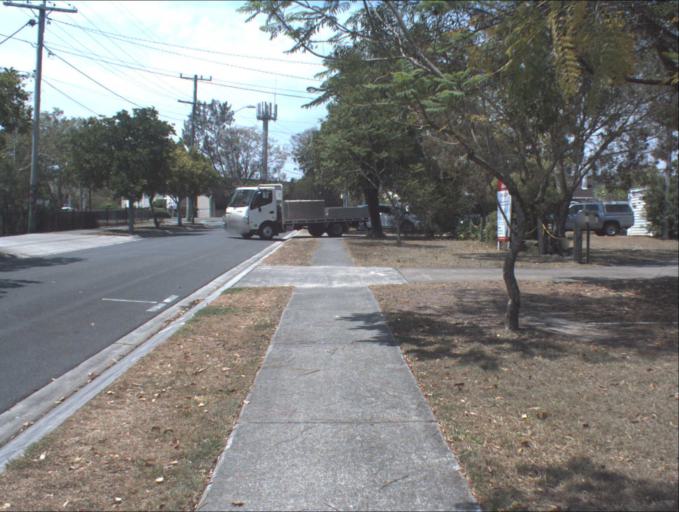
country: AU
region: Queensland
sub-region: Logan
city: Slacks Creek
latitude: -27.6641
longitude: 153.1796
